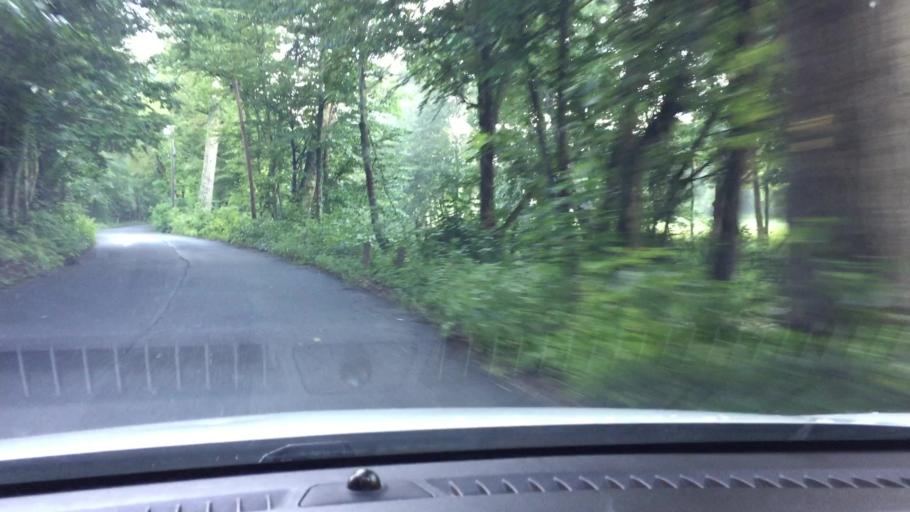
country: US
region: Massachusetts
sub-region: Hampshire County
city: Chesterfield
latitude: 42.3393
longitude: -72.9474
